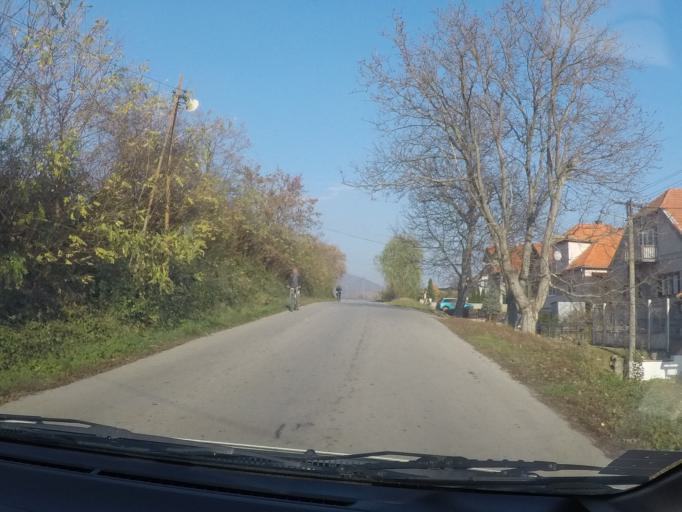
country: SK
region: Banskobystricky
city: Nova Bana
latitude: 48.3899
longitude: 18.6205
